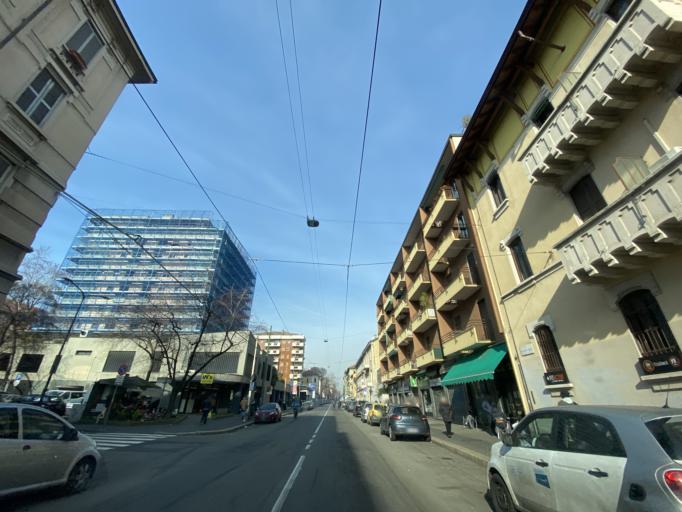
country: IT
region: Lombardy
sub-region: Citta metropolitana di Milano
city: Bresso
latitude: 45.5147
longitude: 9.1731
